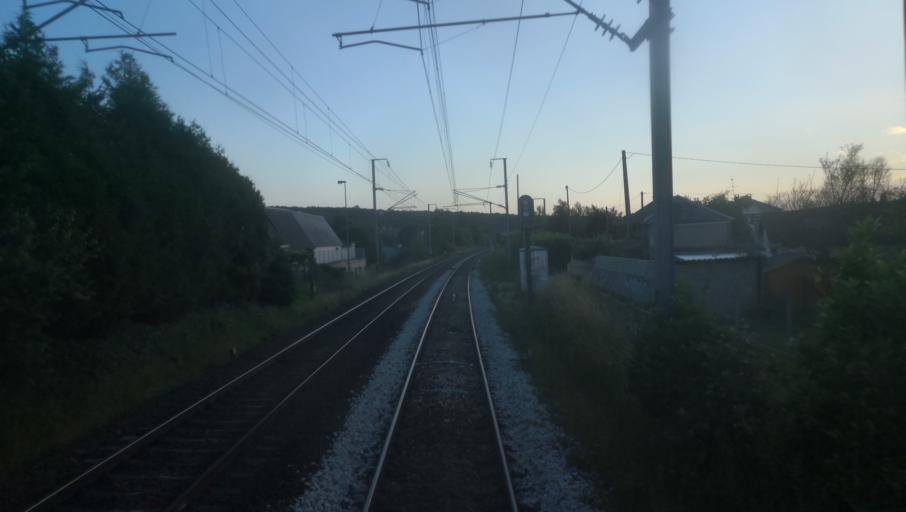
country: FR
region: Haute-Normandie
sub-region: Departement de l'Eure
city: Arnieres-sur-Iton
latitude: 48.9964
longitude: 1.1022
